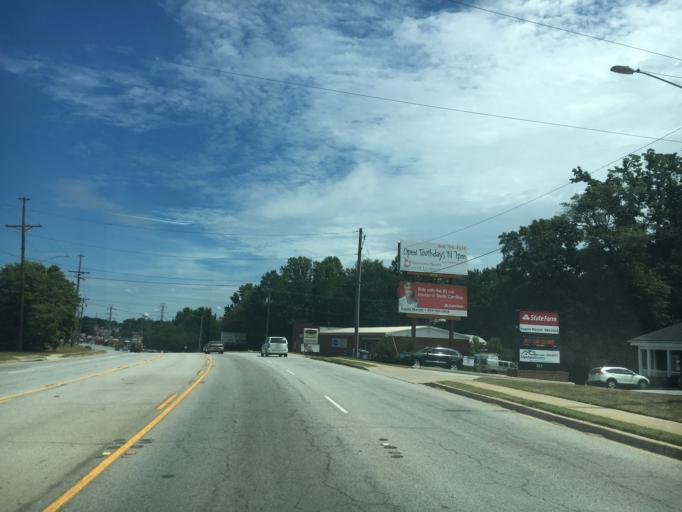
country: US
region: South Carolina
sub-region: Laurens County
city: Laurens
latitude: 34.5053
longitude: -82.0194
